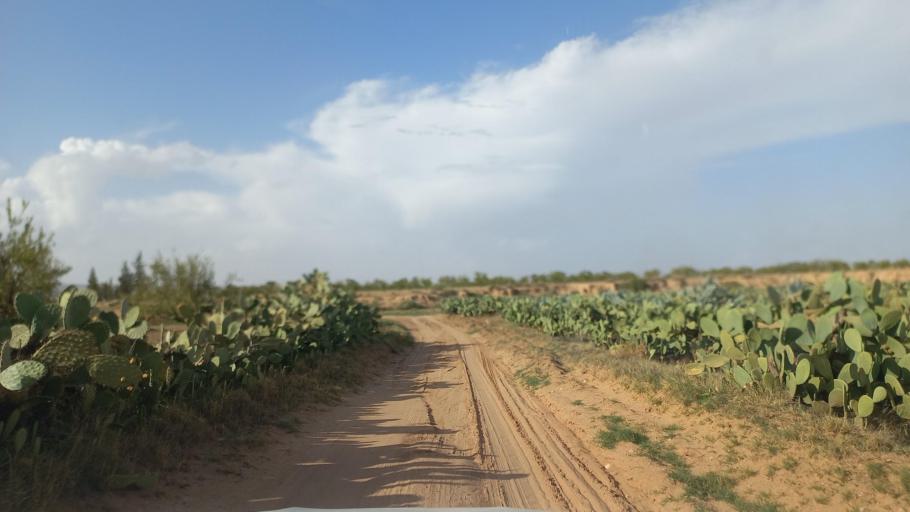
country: TN
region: Al Qasrayn
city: Kasserine
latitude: 35.2279
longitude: 8.9678
